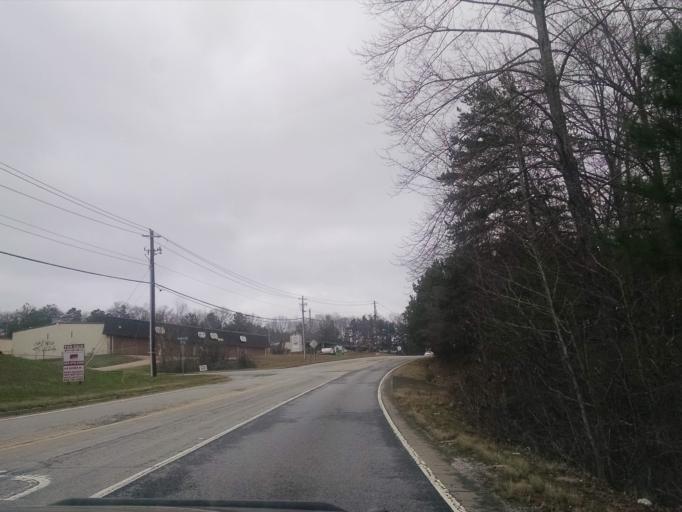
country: US
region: Georgia
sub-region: Gwinnett County
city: Suwanee
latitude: 34.0753
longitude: -84.0493
